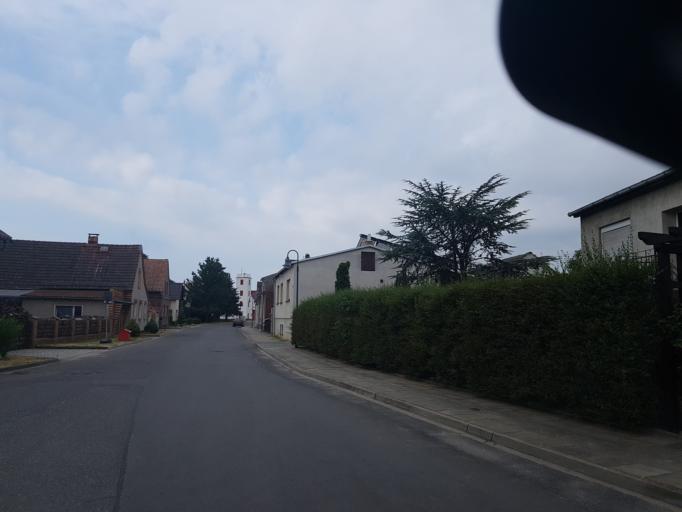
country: DE
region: Brandenburg
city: Doberlug-Kirchhain
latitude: 51.6920
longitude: 13.5145
